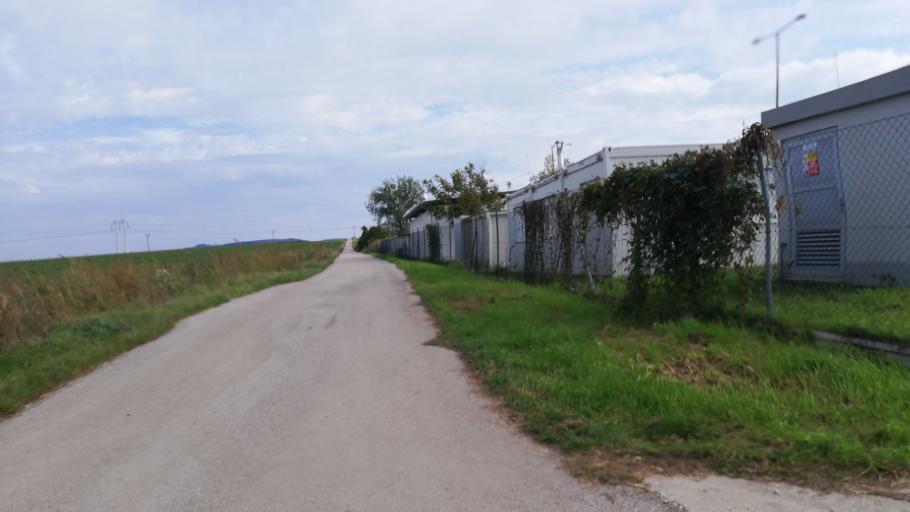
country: CZ
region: South Moravian
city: Sudomerice
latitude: 48.8501
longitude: 17.2527
